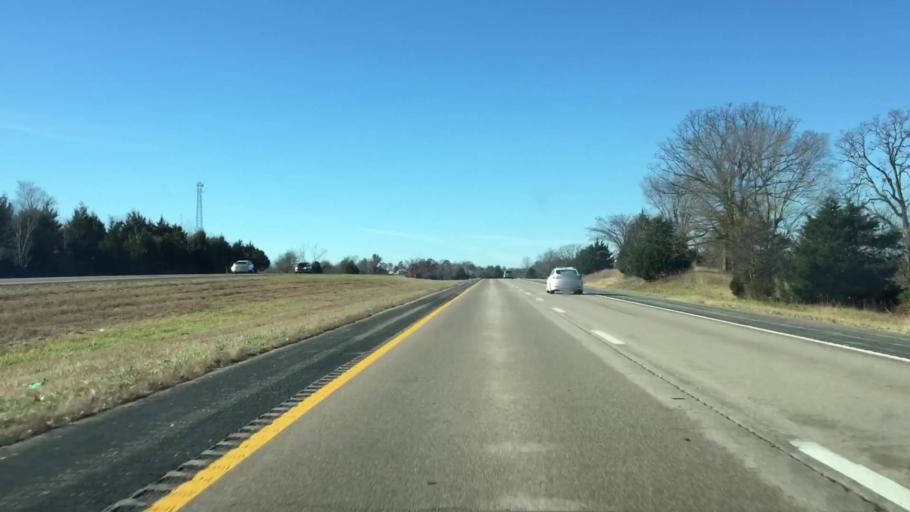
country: US
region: Missouri
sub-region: Miller County
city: Eldon
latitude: 38.3730
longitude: -92.4536
